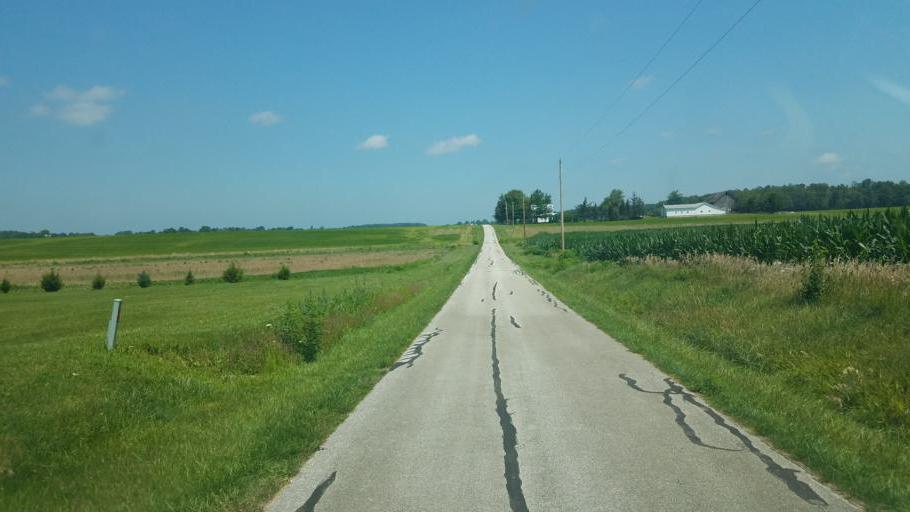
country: US
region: Ohio
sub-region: Sandusky County
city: Mount Carmel
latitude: 41.1515
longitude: -82.9766
